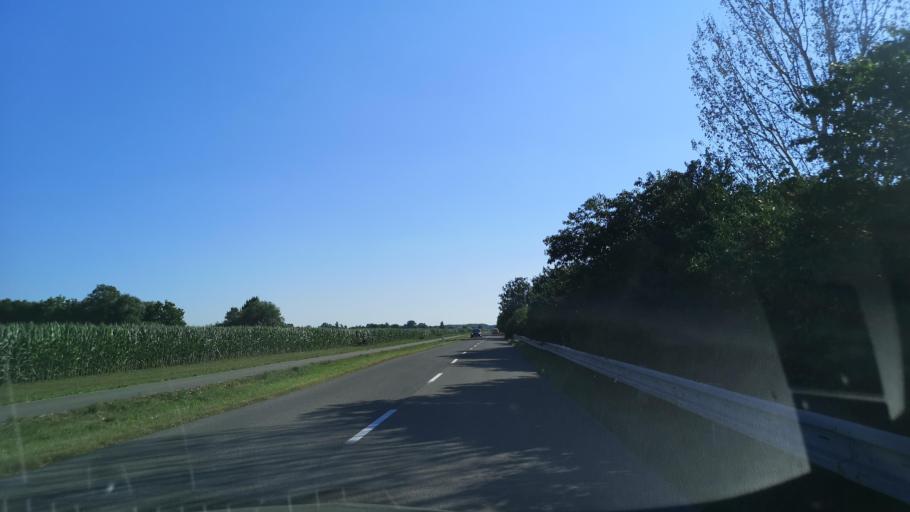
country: SK
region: Trnavsky
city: Dunajska Streda
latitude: 48.0376
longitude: 17.5536
